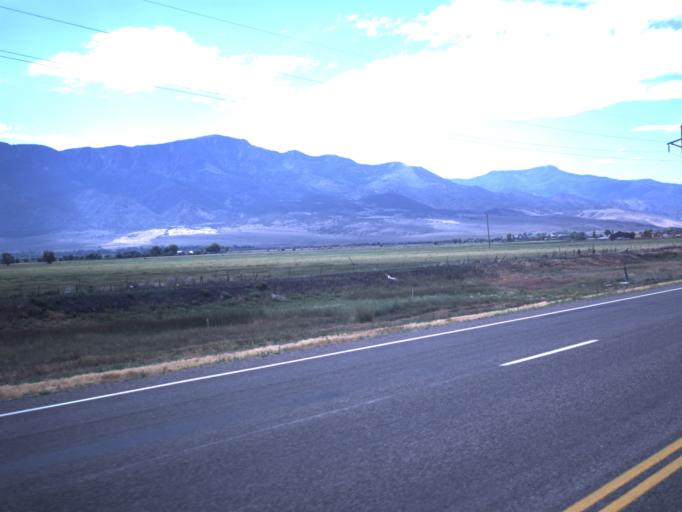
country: US
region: Utah
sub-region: Sevier County
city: Richfield
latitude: 38.7439
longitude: -112.0908
